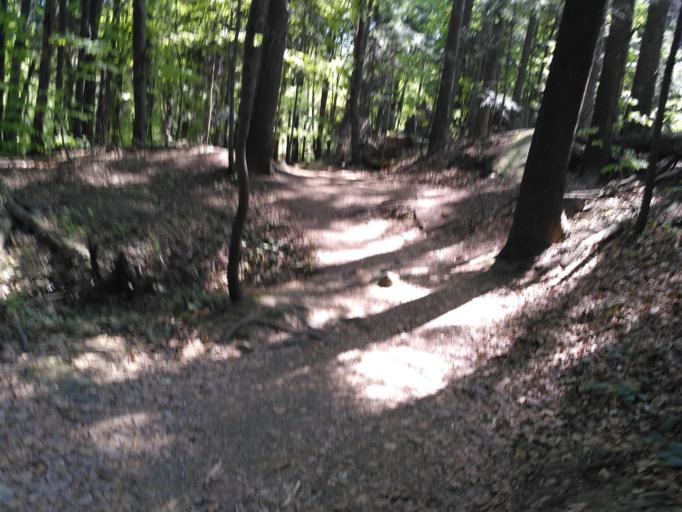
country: PL
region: Subcarpathian Voivodeship
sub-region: Powiat krosnienski
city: Korczyna
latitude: 49.7429
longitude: 21.8078
